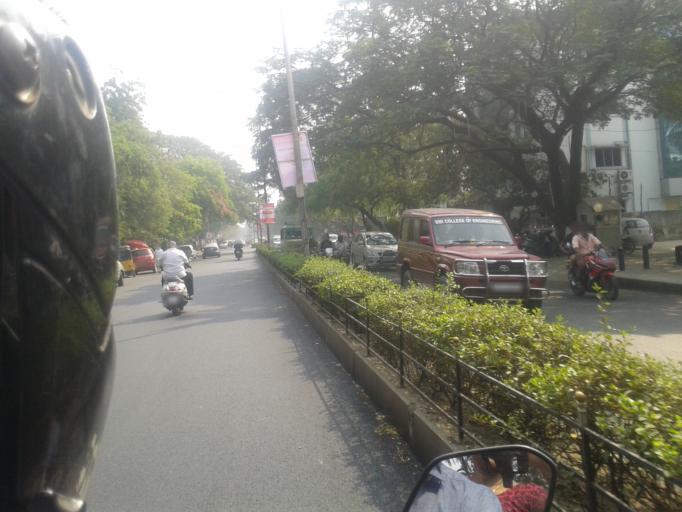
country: IN
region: Tamil Nadu
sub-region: Chennai
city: Chetput
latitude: 13.0825
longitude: 80.2088
